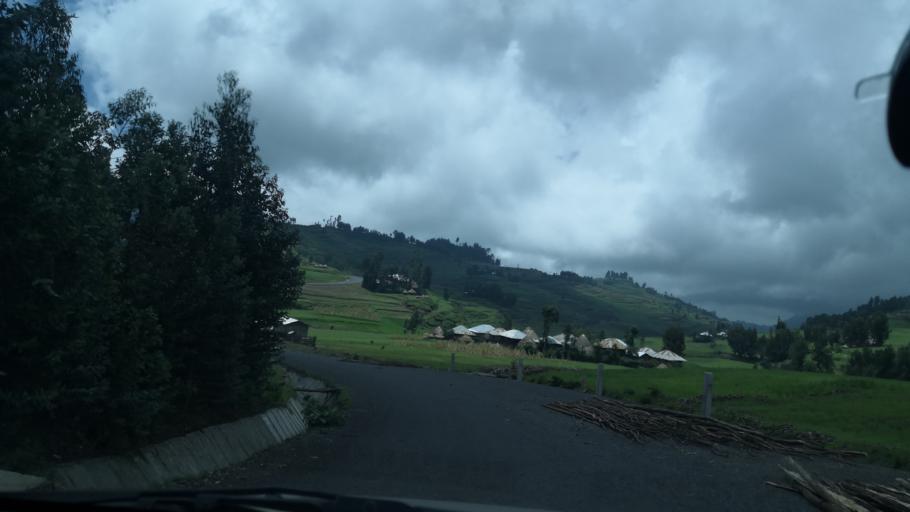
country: ET
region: Amhara
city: Kemise
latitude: 10.3606
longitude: 39.8353
